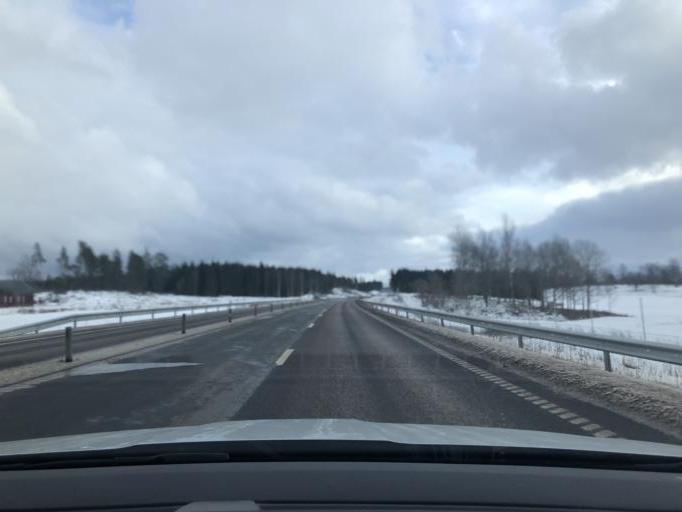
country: SE
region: OEstergoetland
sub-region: Motala Kommun
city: Borensberg
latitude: 58.5888
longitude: 15.1826
